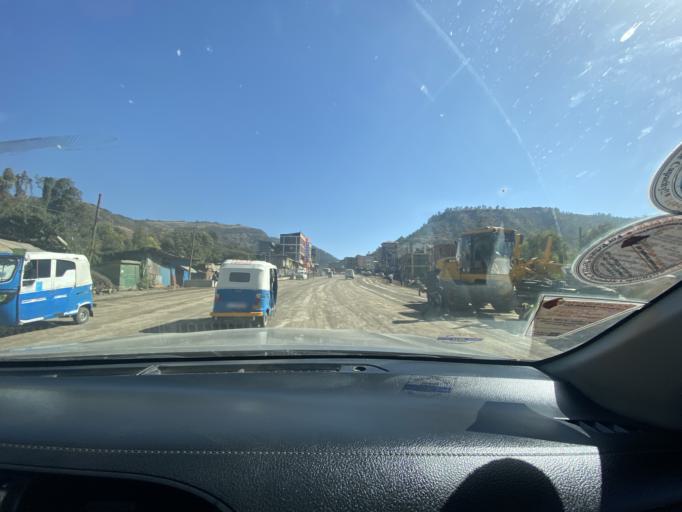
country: ET
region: Amhara
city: Robit
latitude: 11.8291
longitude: 39.5982
